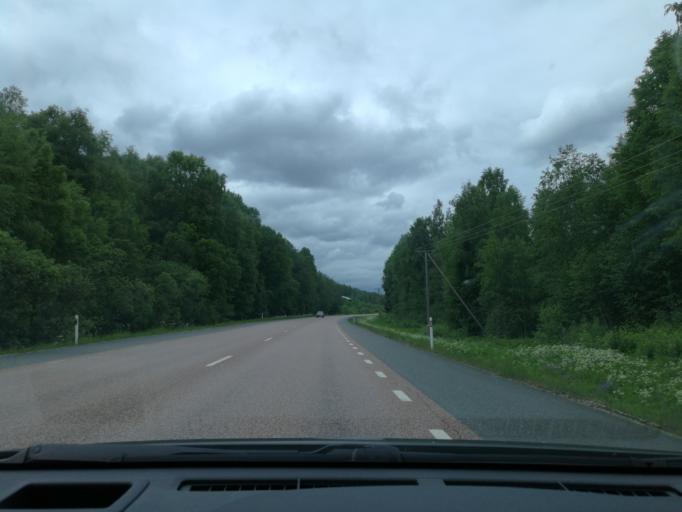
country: SE
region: Vaestmanland
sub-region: Fagersta Kommun
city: Fagersta
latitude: 59.9875
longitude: 15.6775
